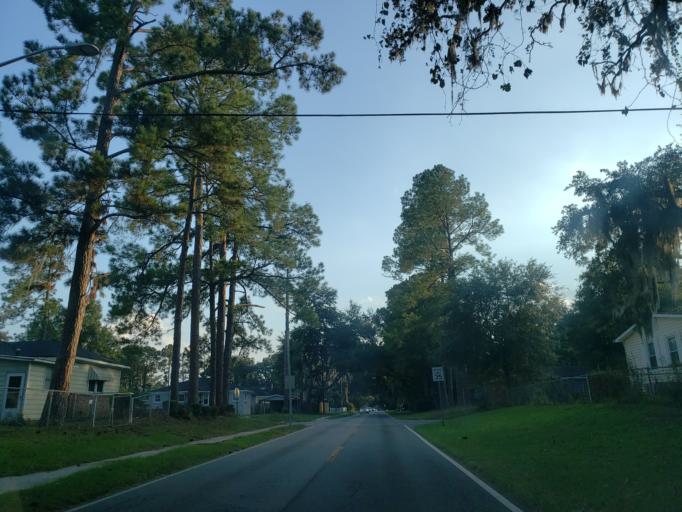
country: US
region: Georgia
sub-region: Chatham County
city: Thunderbolt
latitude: 32.0528
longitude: -81.0742
